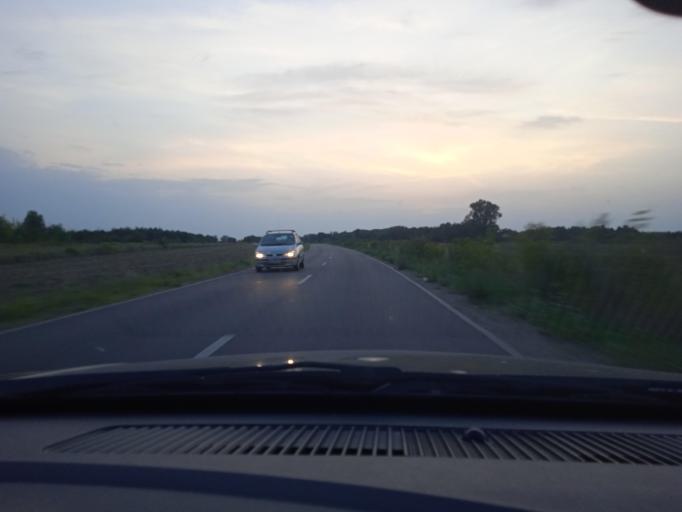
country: PL
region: Masovian Voivodeship
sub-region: Powiat nowodworski
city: Pomiechowek
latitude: 52.4643
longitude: 20.7094
